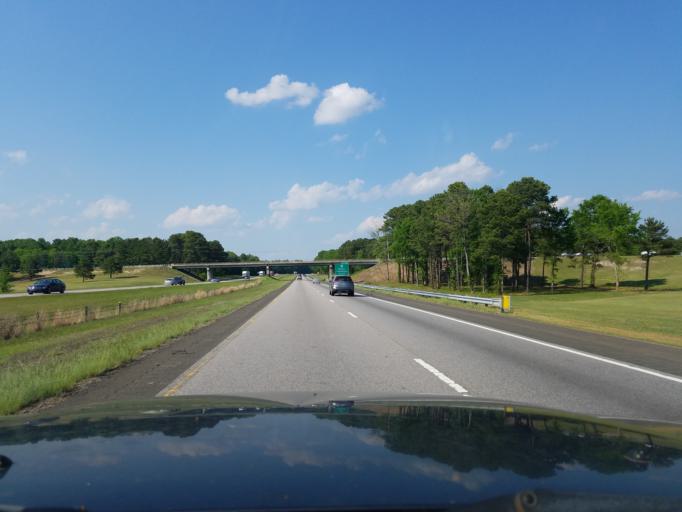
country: US
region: North Carolina
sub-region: Granville County
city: Butner
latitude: 36.1188
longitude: -78.7467
